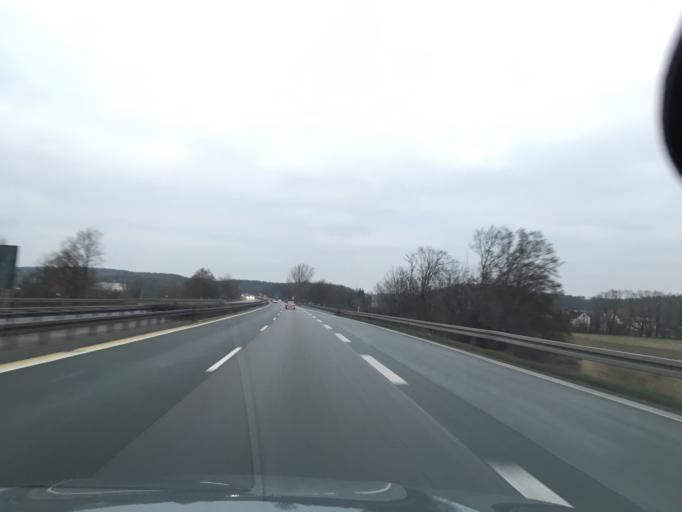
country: DE
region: Bavaria
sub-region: Regierungsbezirk Mittelfranken
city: Gremsdorf
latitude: 49.7016
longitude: 10.8542
